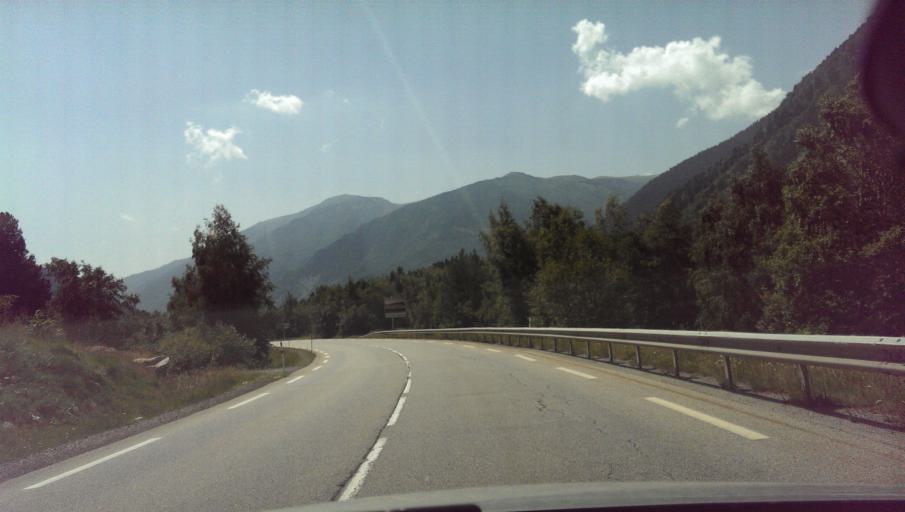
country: AD
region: Encamp
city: Pas de la Casa
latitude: 42.5326
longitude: 1.8216
